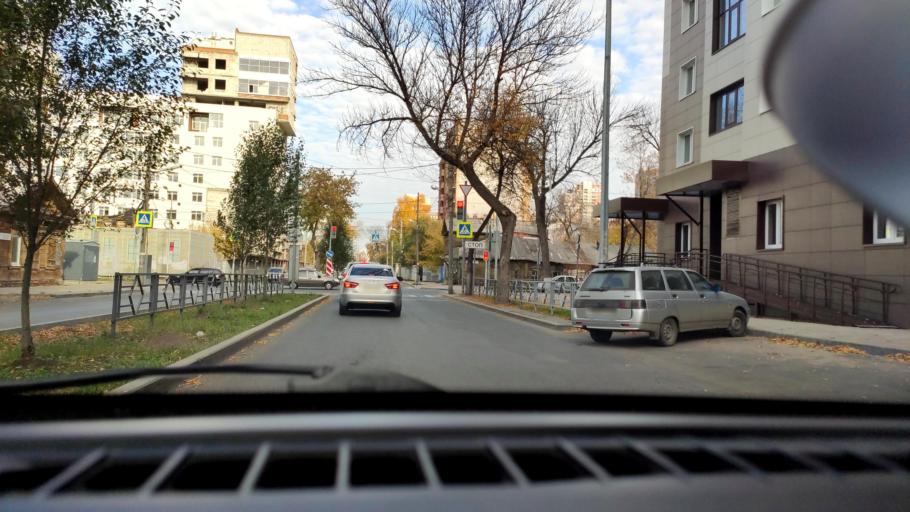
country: RU
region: Samara
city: Samara
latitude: 53.1998
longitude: 50.1184
